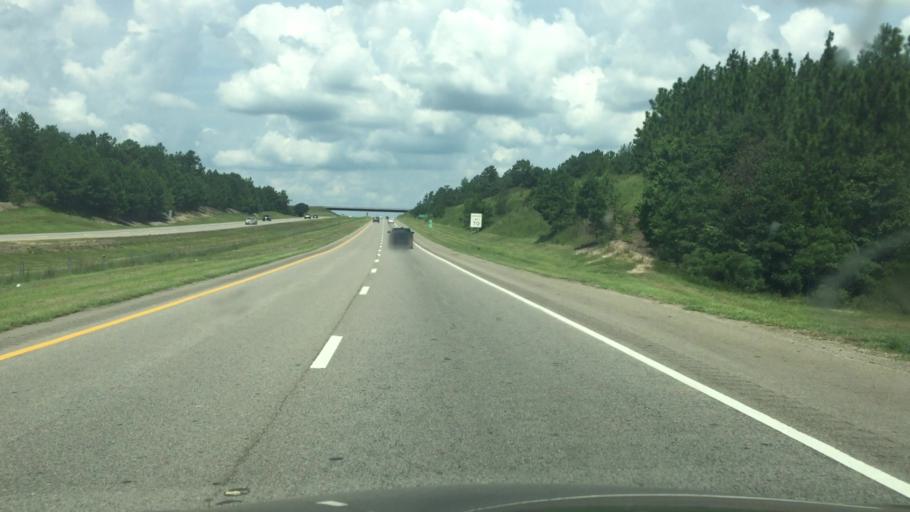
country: US
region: North Carolina
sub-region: Richmond County
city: Ellerbe
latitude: 35.1822
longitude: -79.7159
